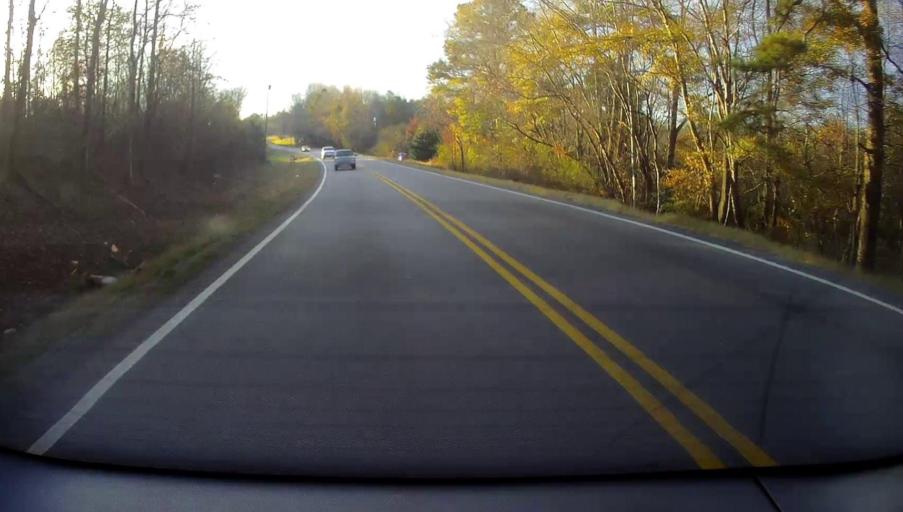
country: US
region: Alabama
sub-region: Saint Clair County
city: Steele
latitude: 34.0673
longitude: -86.2644
